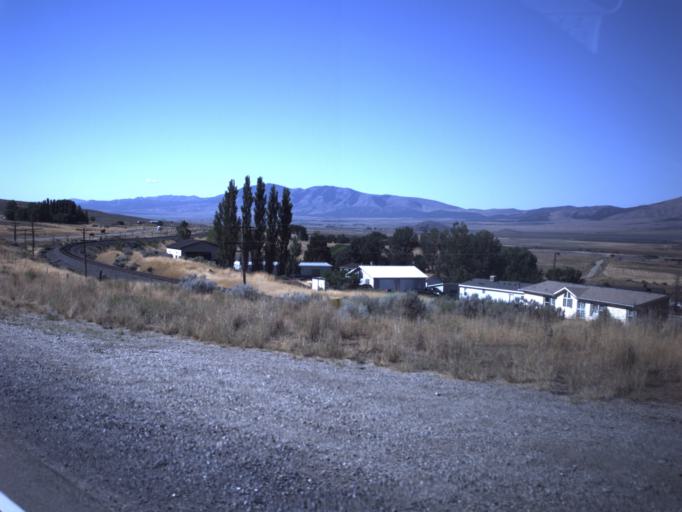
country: US
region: Utah
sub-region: Tooele County
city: Tooele
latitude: 40.4494
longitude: -112.3634
